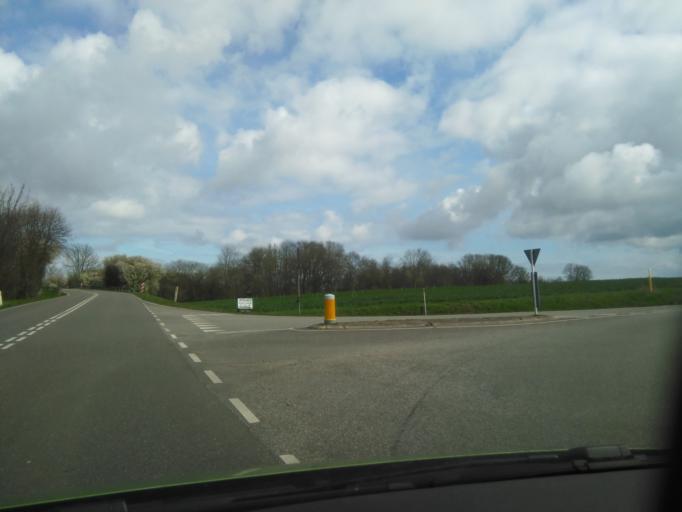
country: DK
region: South Denmark
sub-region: Middelfart Kommune
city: Strib
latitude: 55.5160
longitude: 9.7851
